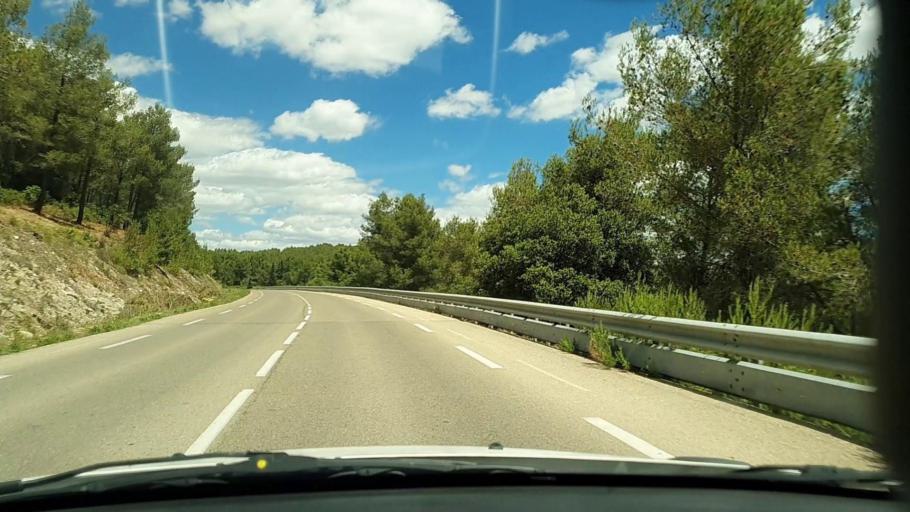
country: FR
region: Languedoc-Roussillon
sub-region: Departement du Gard
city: Poulx
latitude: 43.8794
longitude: 4.4171
